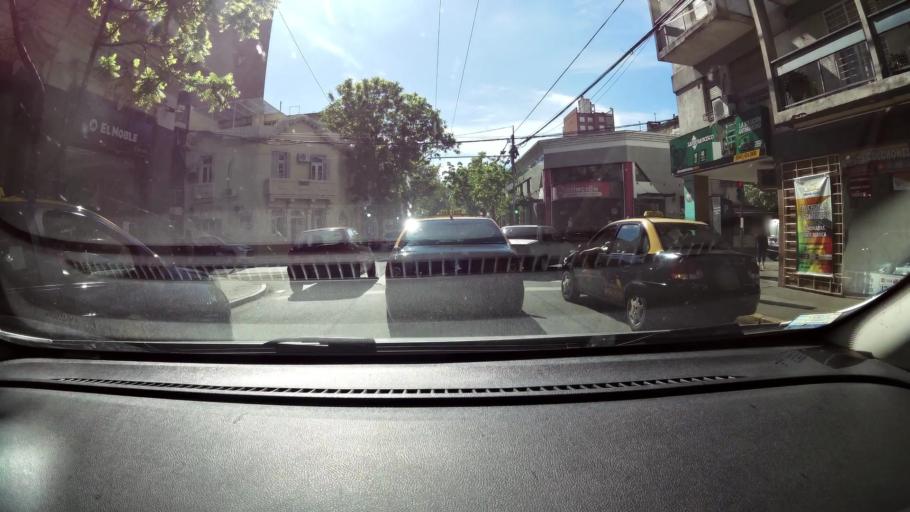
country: AR
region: Santa Fe
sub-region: Departamento de Rosario
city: Rosario
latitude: -32.9500
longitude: -60.6480
